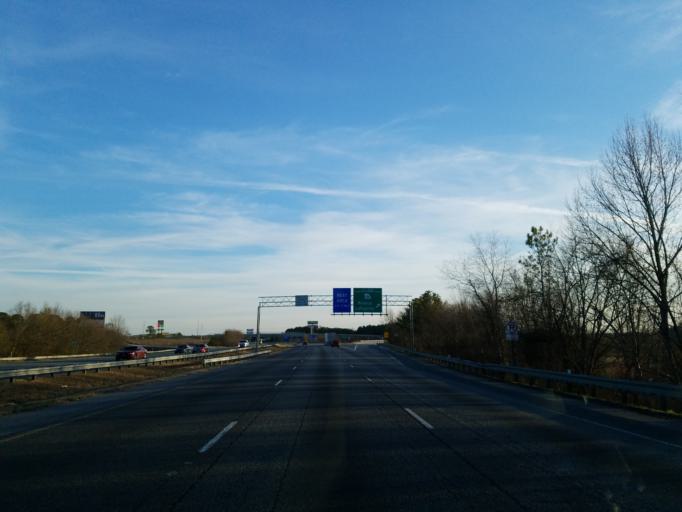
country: US
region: Georgia
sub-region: Gordon County
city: Calhoun
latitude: 34.5817
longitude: -84.9522
